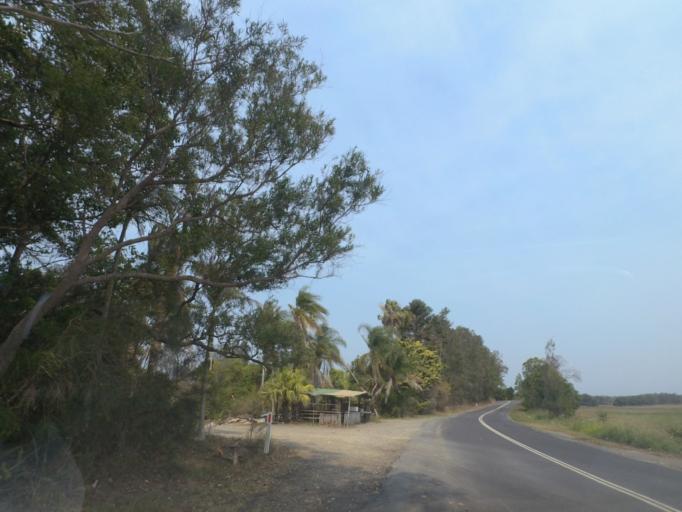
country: AU
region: New South Wales
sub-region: Tweed
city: Burringbar
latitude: -28.4537
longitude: 153.5344
